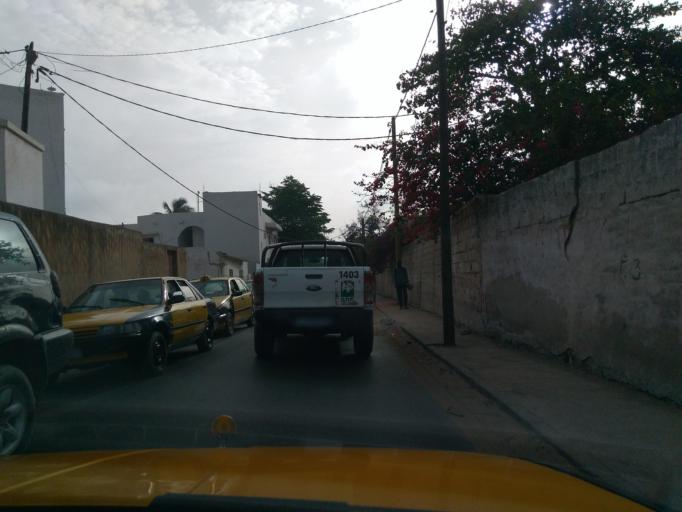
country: SN
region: Dakar
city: Grand Dakar
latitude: 14.7255
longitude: -17.4392
